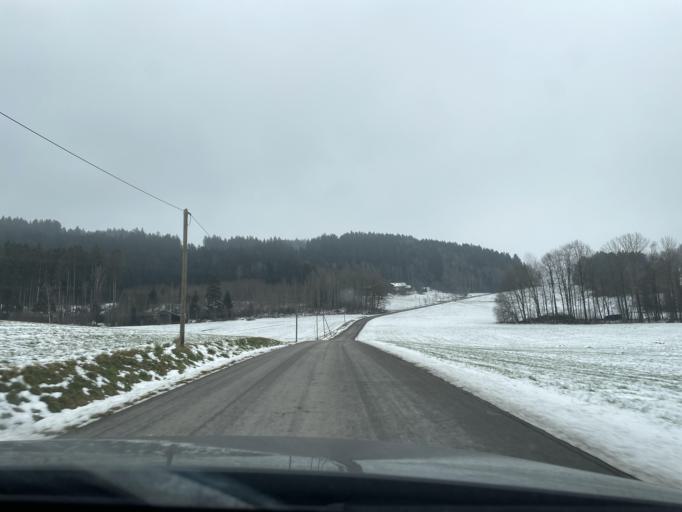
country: DE
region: Bavaria
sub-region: Lower Bavaria
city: Kollnburg
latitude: 49.0179
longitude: 12.8900
